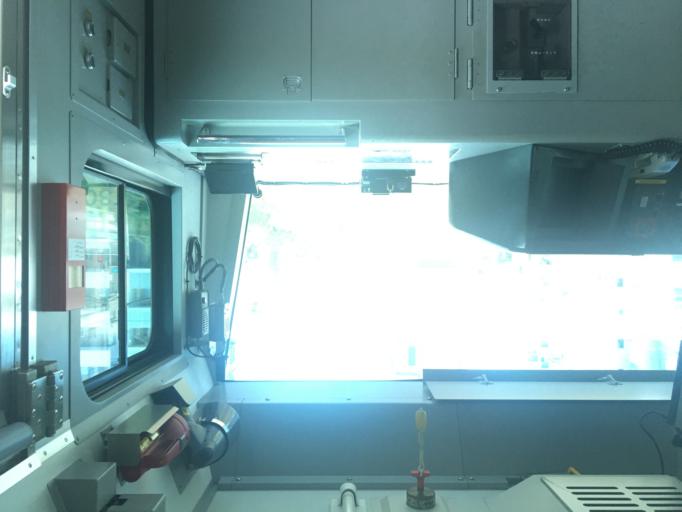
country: JP
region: Tokyo
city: Hino
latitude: 35.6995
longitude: 139.4068
